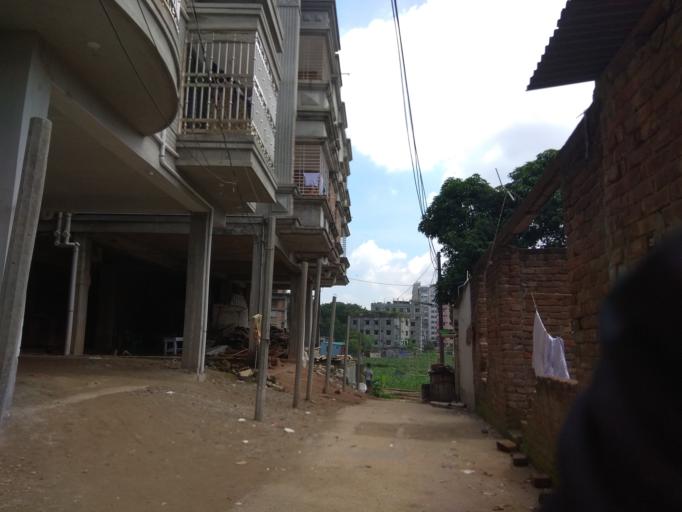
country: BD
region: Dhaka
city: Tungi
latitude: 23.8249
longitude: 90.3872
